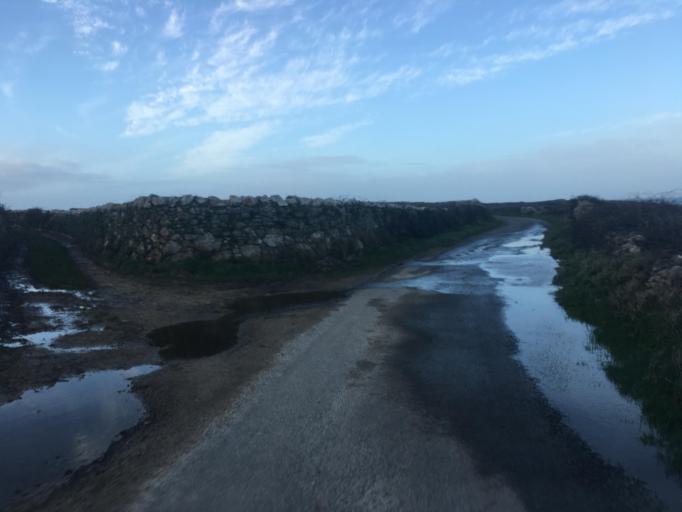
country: FR
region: Lower Normandy
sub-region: Departement de la Manche
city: Beaumont-Hague
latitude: 49.7222
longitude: -1.9225
